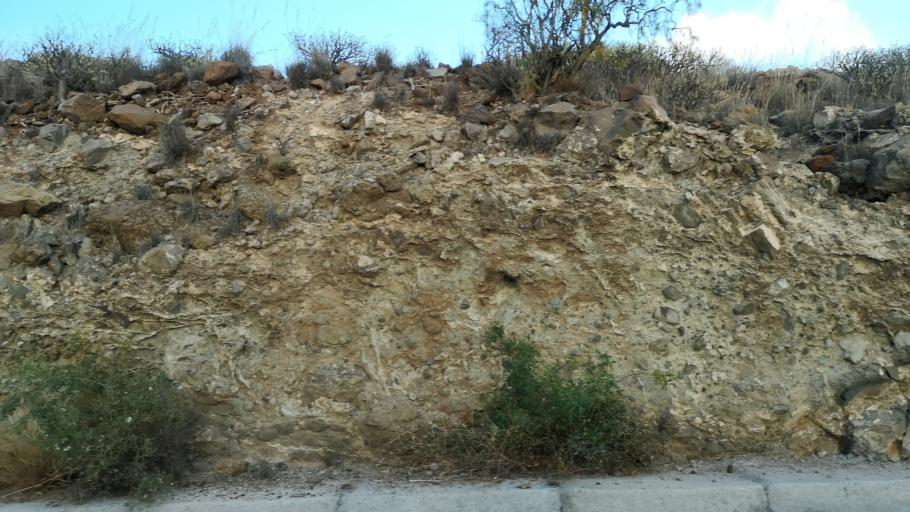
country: ES
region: Canary Islands
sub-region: Provincia de Santa Cruz de Tenerife
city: Alajero
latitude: 28.0399
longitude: -17.2266
